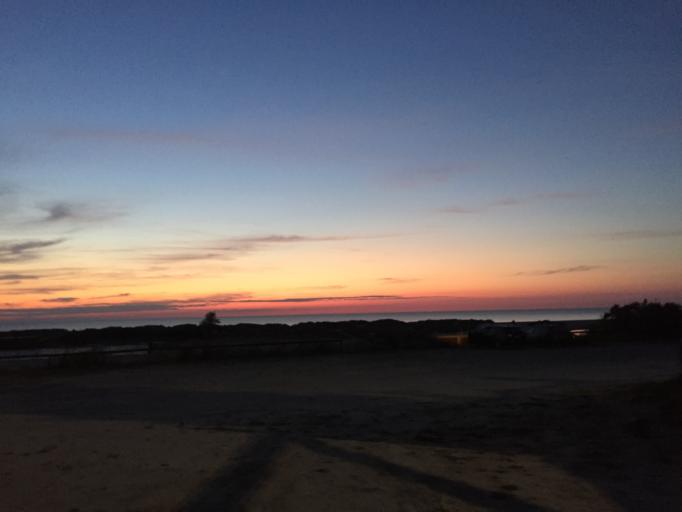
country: RU
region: Kaliningrad
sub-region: Gorod Kaliningrad
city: Yantarnyy
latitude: 54.8840
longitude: 19.9352
